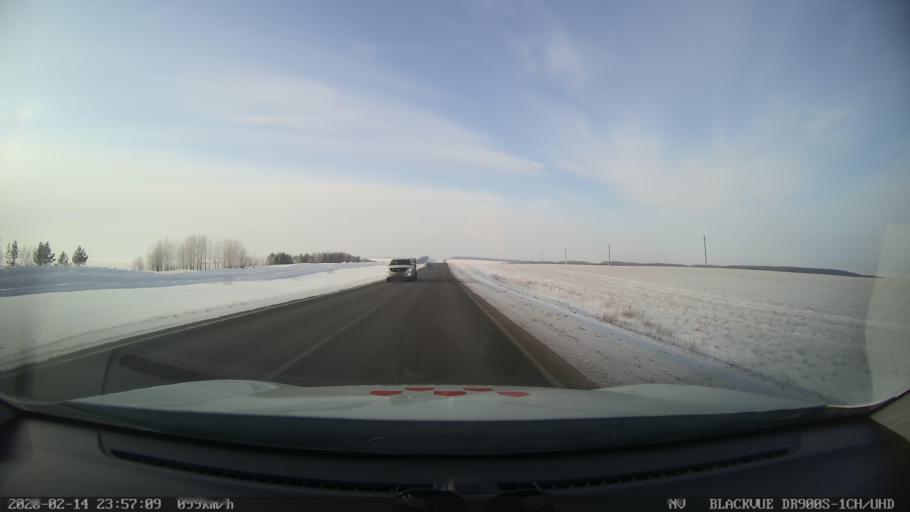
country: RU
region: Tatarstan
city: Kuybyshevskiy Zaton
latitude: 55.3319
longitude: 49.1162
